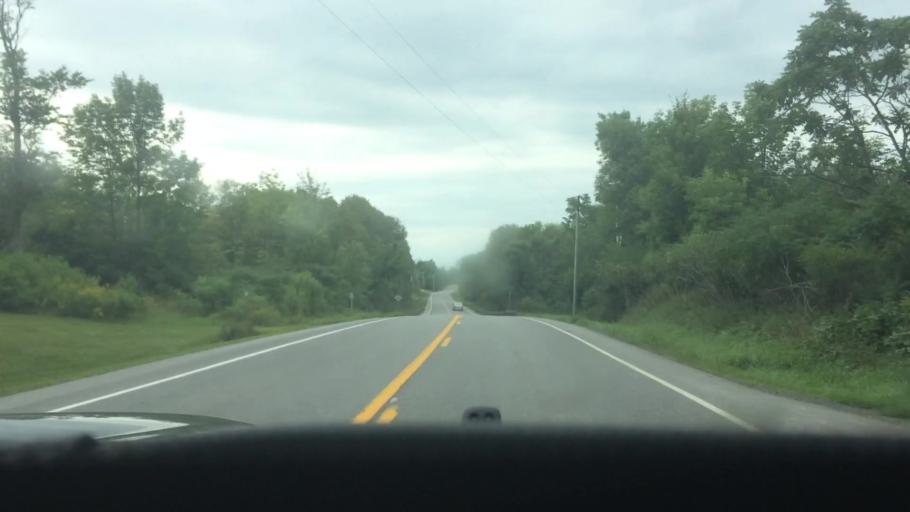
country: US
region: New York
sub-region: St. Lawrence County
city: Canton
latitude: 44.5132
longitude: -75.3399
